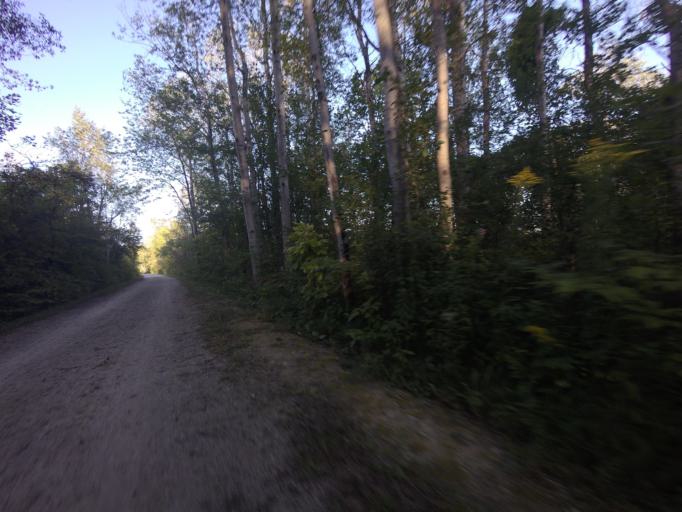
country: CA
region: Ontario
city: Brampton
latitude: 43.8256
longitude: -79.9130
